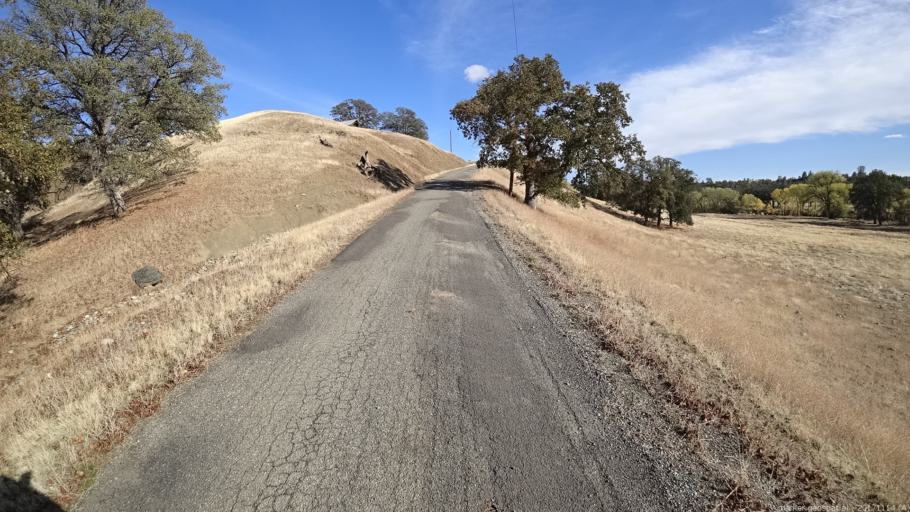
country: US
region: California
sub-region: Shasta County
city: Shasta
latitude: 40.3694
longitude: -122.5760
